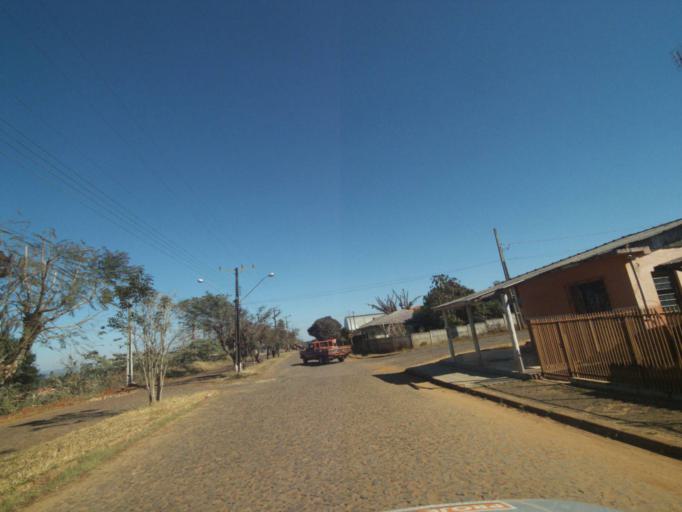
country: BR
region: Parana
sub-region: Reserva
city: Reserva
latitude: -24.6214
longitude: -50.6384
